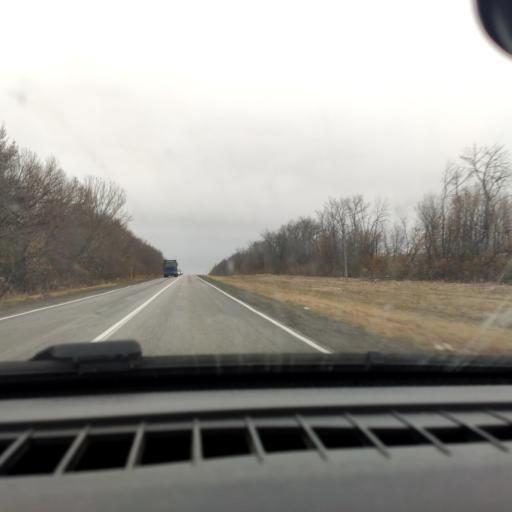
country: RU
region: Voronezj
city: Uryv-Pokrovka
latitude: 51.1072
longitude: 39.0221
